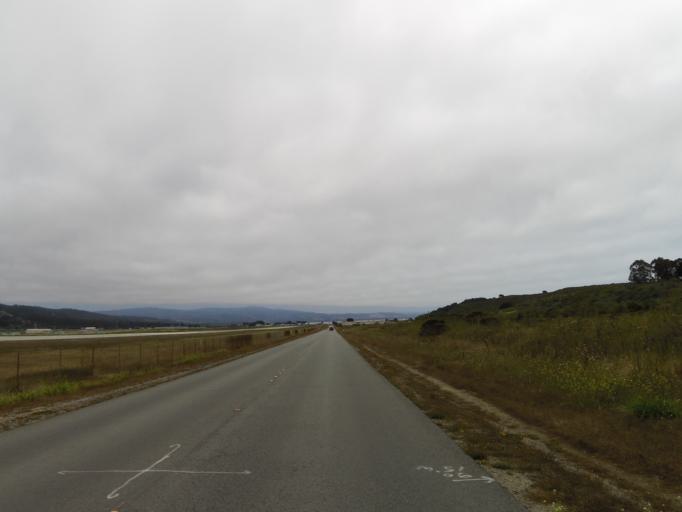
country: US
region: California
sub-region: San Mateo County
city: Moss Beach
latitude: 37.5182
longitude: -122.5086
